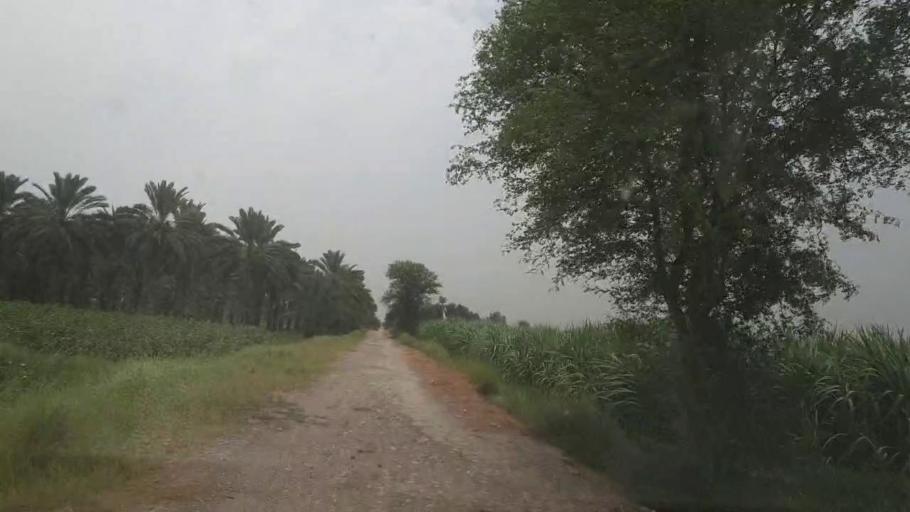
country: PK
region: Sindh
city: Gambat
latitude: 27.4251
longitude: 68.6173
